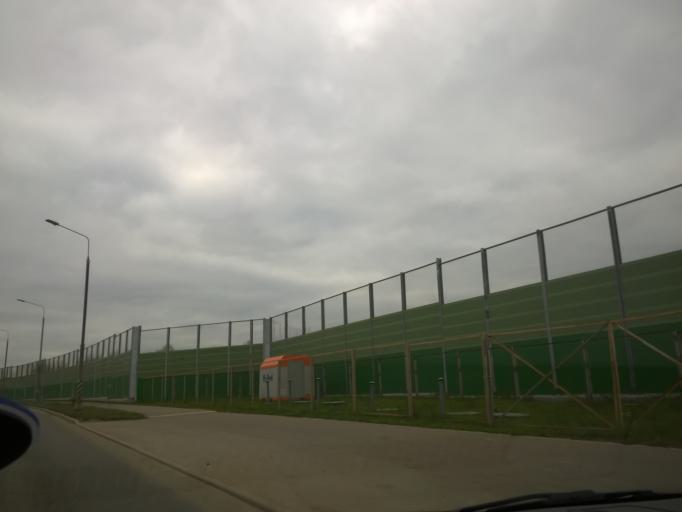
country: RU
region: Moskovskaya
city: Kommunarka
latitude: 55.5507
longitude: 37.4865
